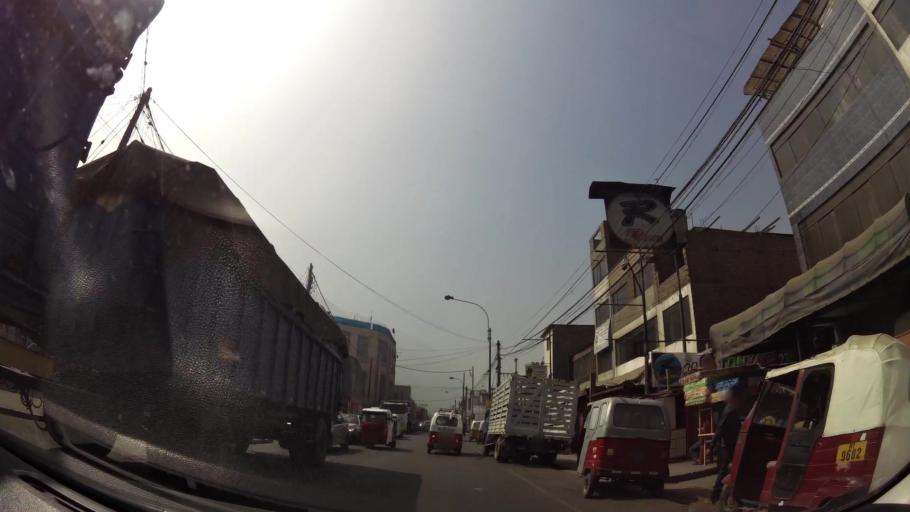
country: PE
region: Lima
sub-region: Lima
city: Asentamiento Humano Nicolas de Pierola
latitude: -11.9330
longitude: -76.6931
